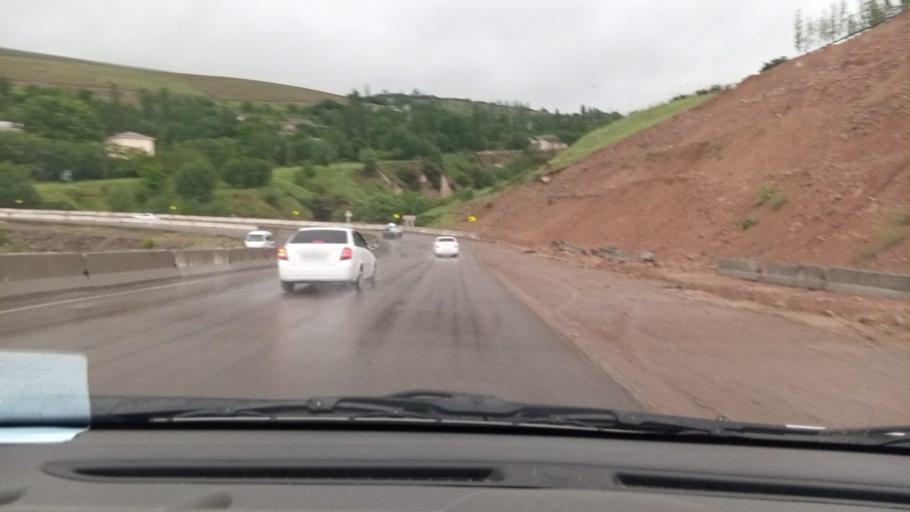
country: UZ
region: Toshkent
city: Angren
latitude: 41.0719
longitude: 70.2357
